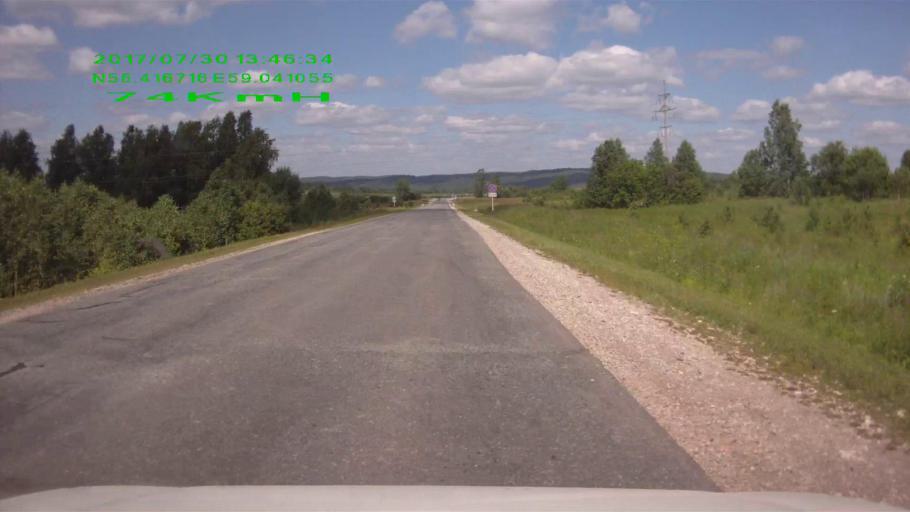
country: RU
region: Sverdlovsk
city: Mikhaylovsk
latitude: 56.4169
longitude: 59.0411
